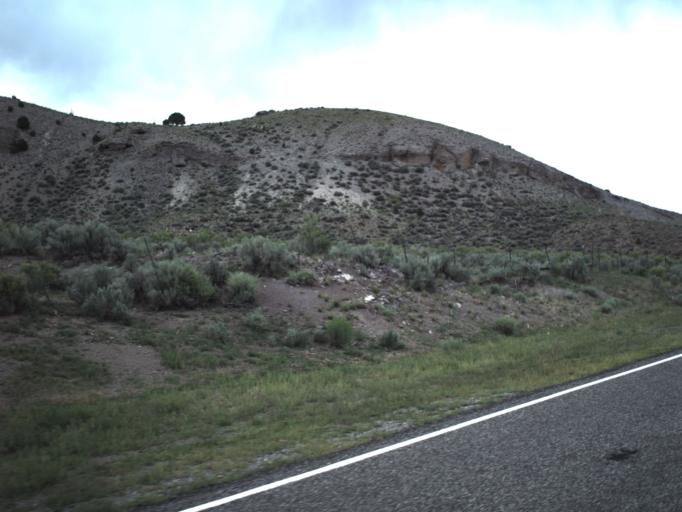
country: US
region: Utah
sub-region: Piute County
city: Junction
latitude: 38.1737
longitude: -112.0628
